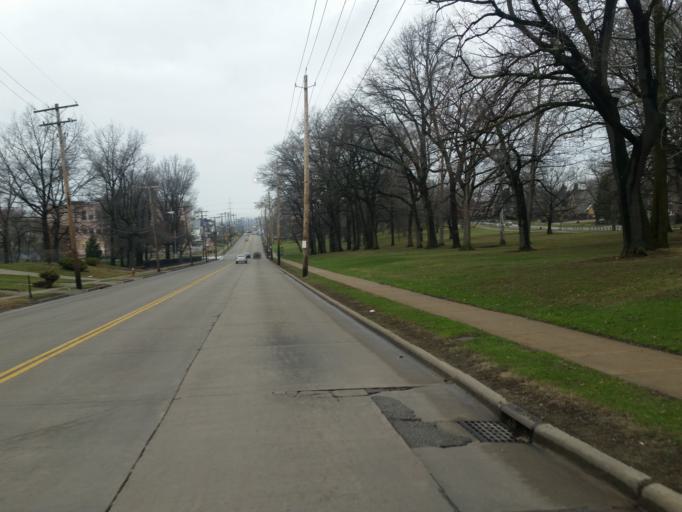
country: US
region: Ohio
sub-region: Cuyahoga County
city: Newburgh Heights
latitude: 41.4705
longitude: -81.6145
